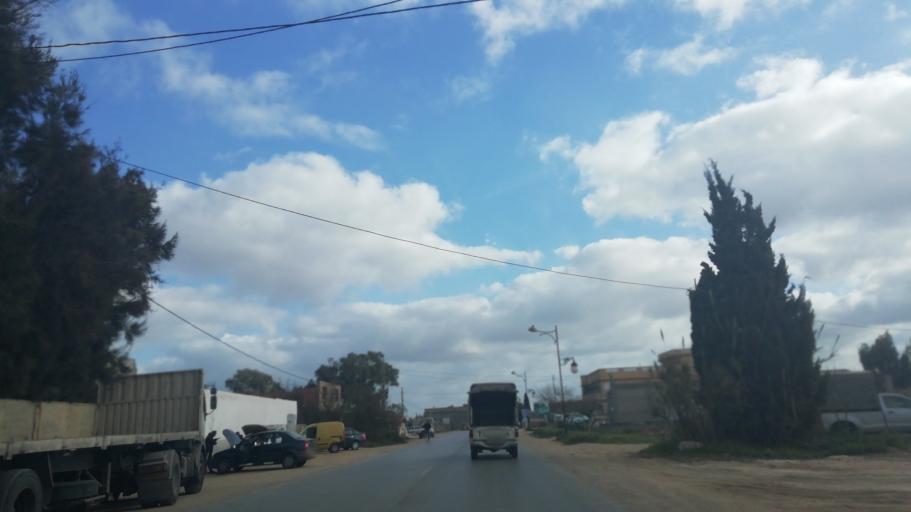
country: DZ
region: Relizane
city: Mazouna
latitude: 36.2666
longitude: 0.6253
